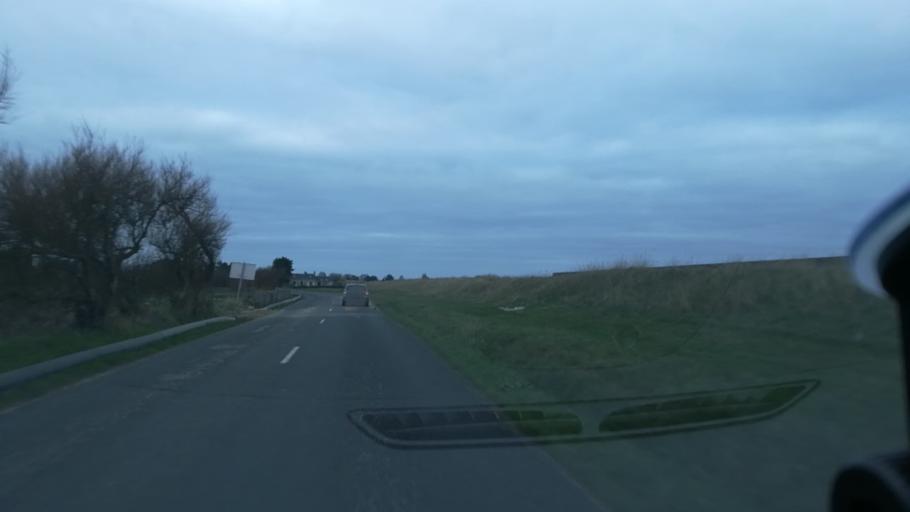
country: FR
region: Lower Normandy
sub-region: Departement de la Manche
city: Reville
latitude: 49.6036
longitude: -1.2597
